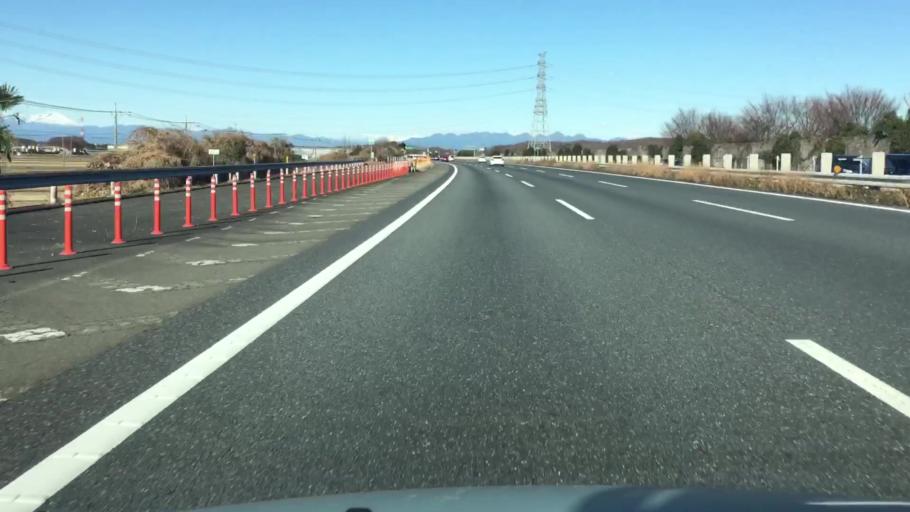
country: JP
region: Saitama
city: Honjo
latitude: 36.1995
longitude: 139.1831
